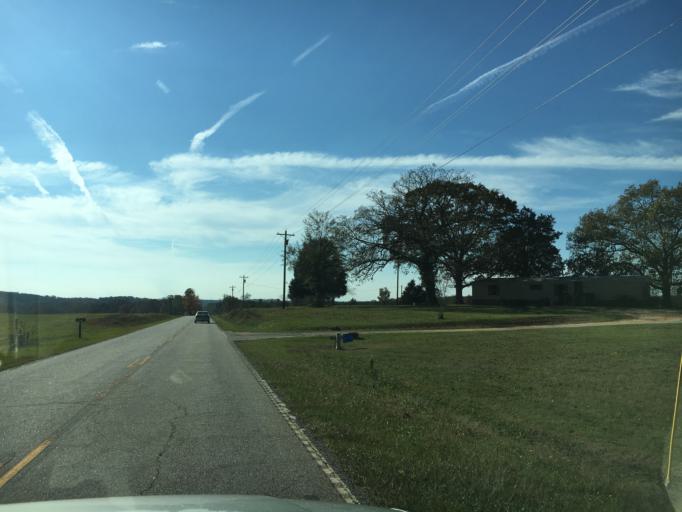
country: US
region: South Carolina
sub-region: Anderson County
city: Iva
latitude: 34.3377
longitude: -82.7626
